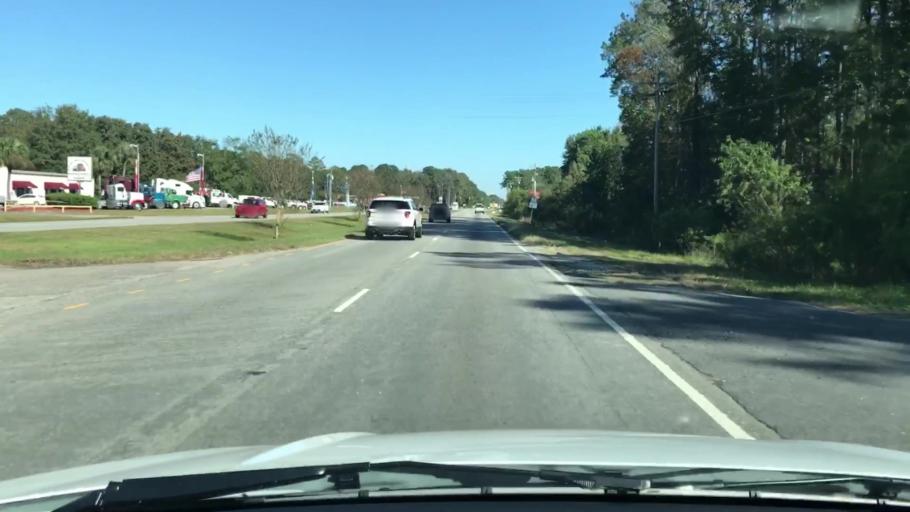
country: US
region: South Carolina
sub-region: Charleston County
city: Ravenel
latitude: 32.7752
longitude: -80.2529
